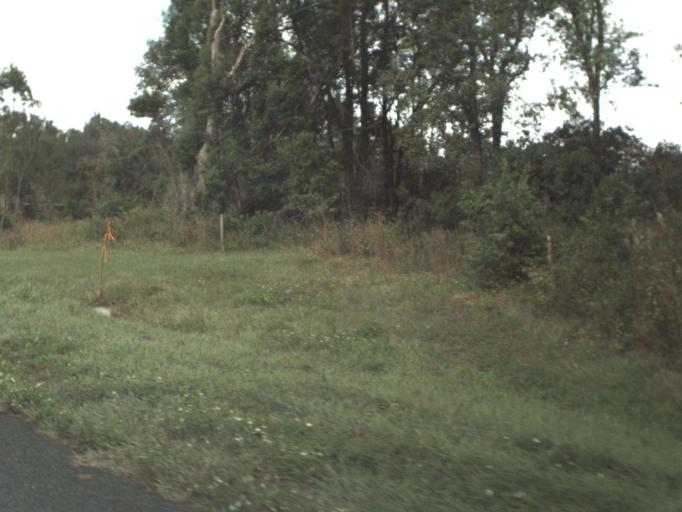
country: US
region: Florida
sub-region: Jefferson County
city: Monticello
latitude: 30.3814
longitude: -83.8215
